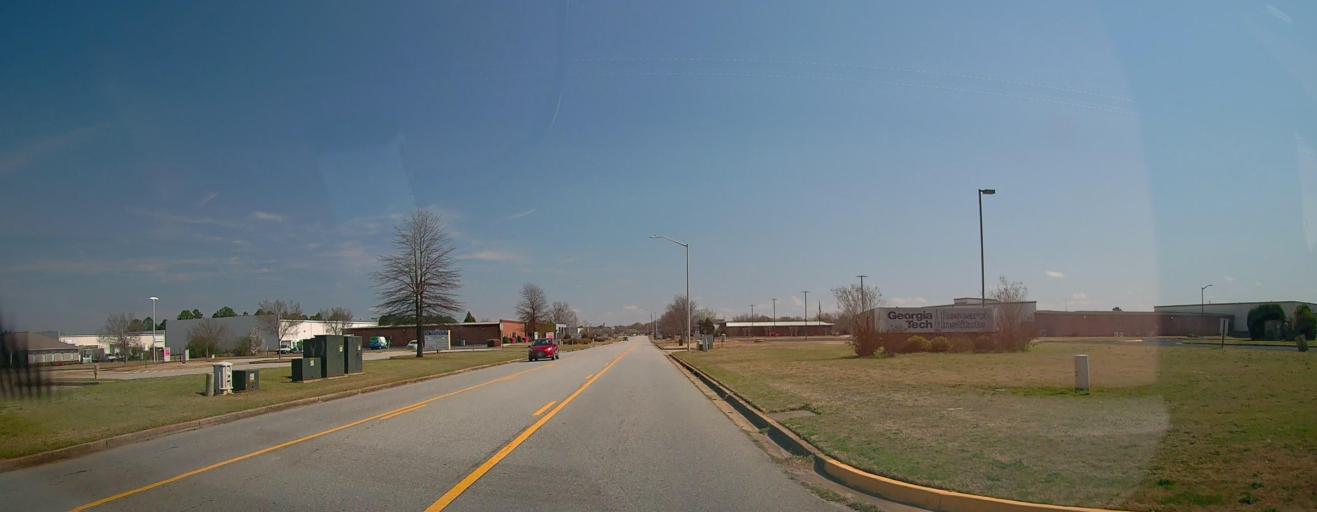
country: US
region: Georgia
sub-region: Houston County
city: Centerville
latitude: 32.6138
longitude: -83.6881
